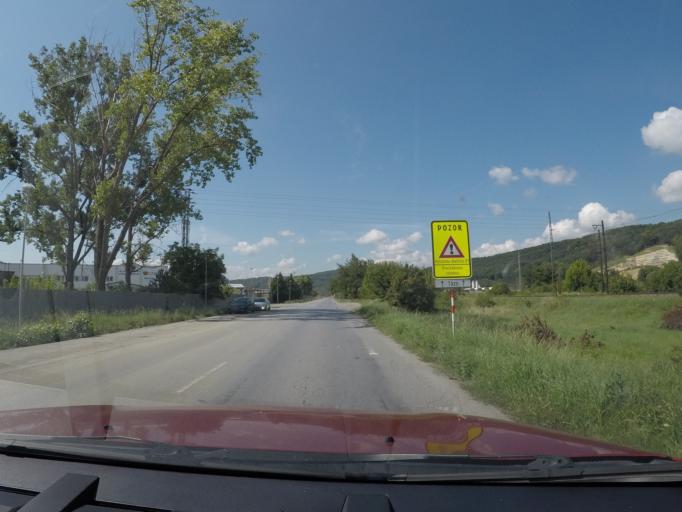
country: SK
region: Presovsky
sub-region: Okres Presov
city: Presov
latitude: 48.9678
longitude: 21.2504
